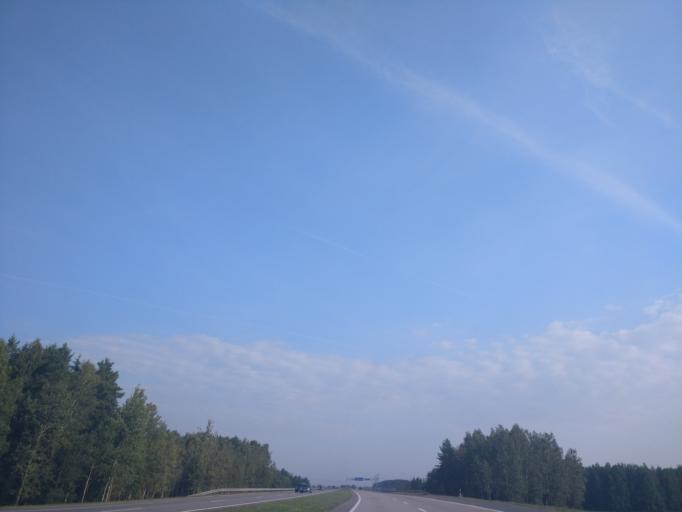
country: BY
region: Minsk
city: Astrashytski Haradok
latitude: 54.0466
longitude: 27.7012
